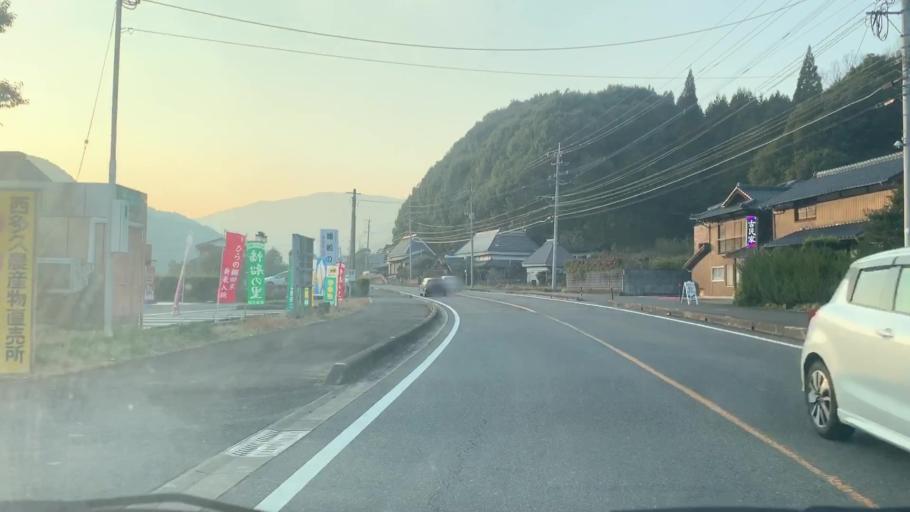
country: JP
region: Saga Prefecture
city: Takeocho-takeo
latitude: 33.2640
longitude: 130.0525
